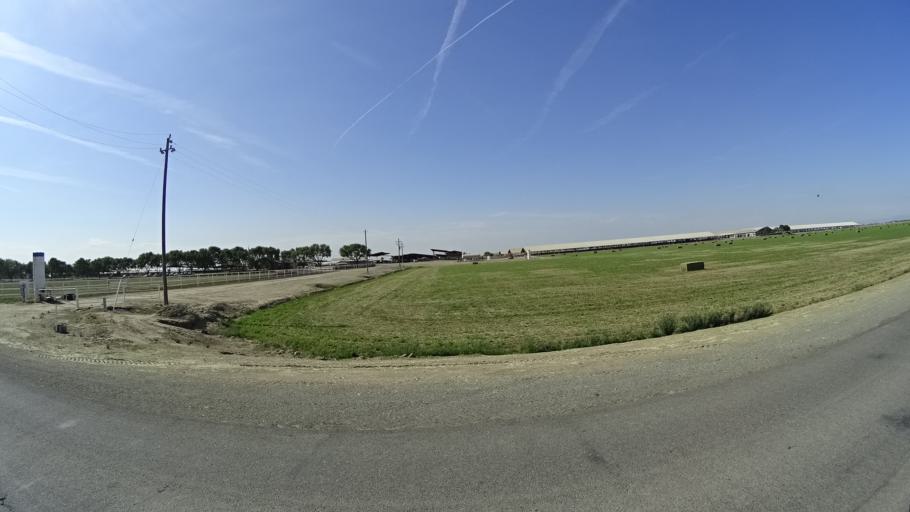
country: US
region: California
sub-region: Kings County
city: Home Garden
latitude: 36.2551
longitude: -119.5691
